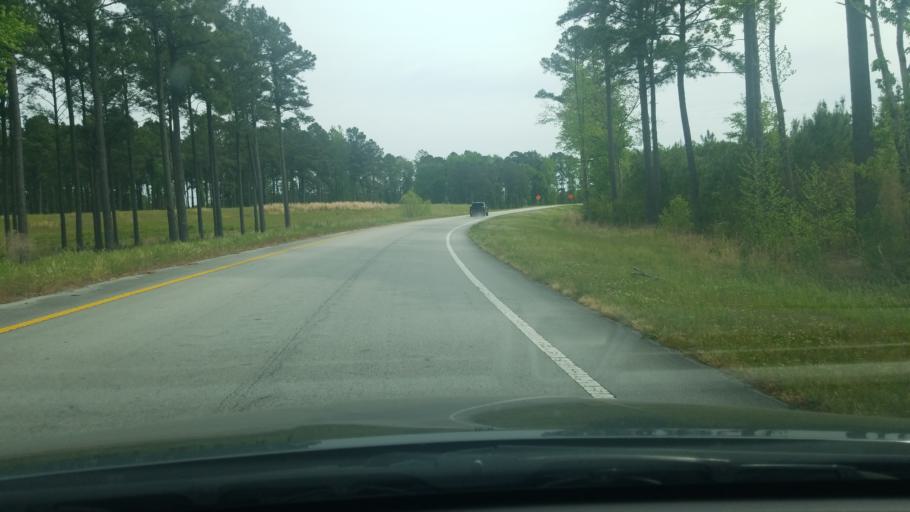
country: US
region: North Carolina
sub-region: Craven County
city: River Bend
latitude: 35.1292
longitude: -77.1519
